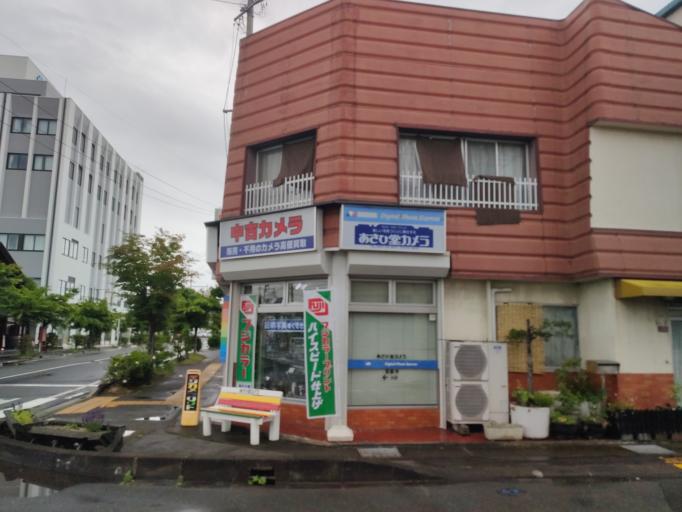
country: JP
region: Nagano
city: Saku
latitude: 36.2301
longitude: 138.4775
